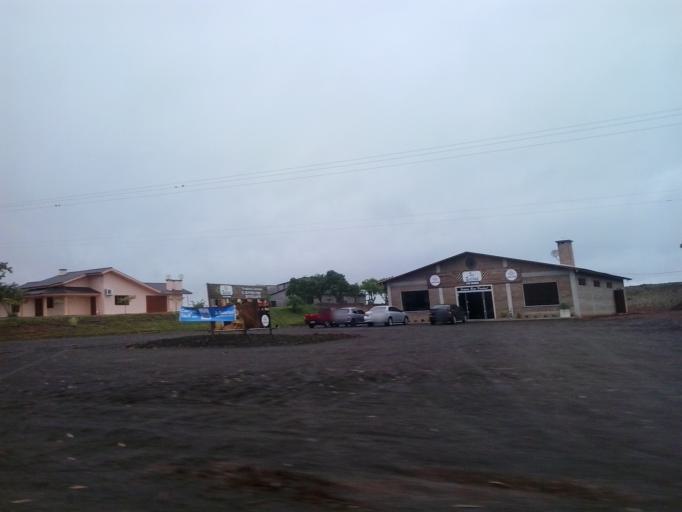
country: BR
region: Rio Grande do Sul
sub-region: Candelaria
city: Candelaria
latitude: -29.7207
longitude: -53.2298
